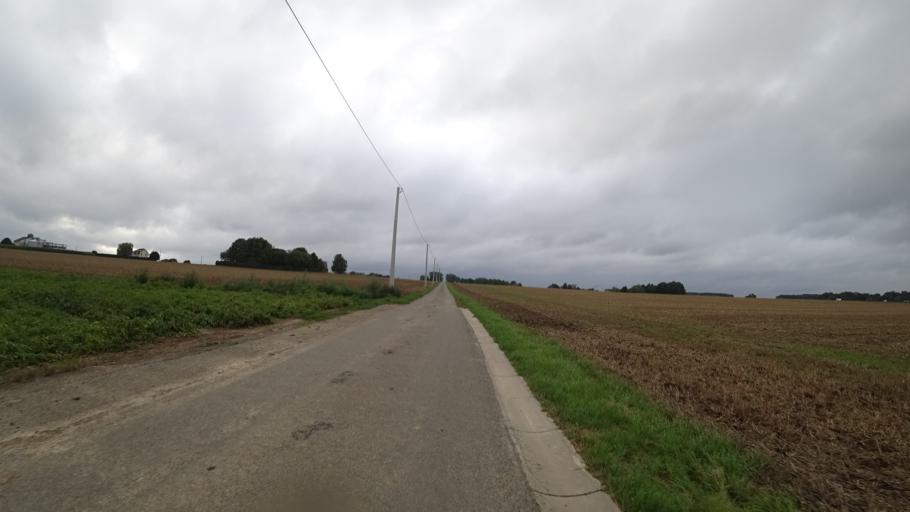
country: BE
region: Wallonia
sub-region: Province du Brabant Wallon
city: Perwez
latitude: 50.5481
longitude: 4.8143
